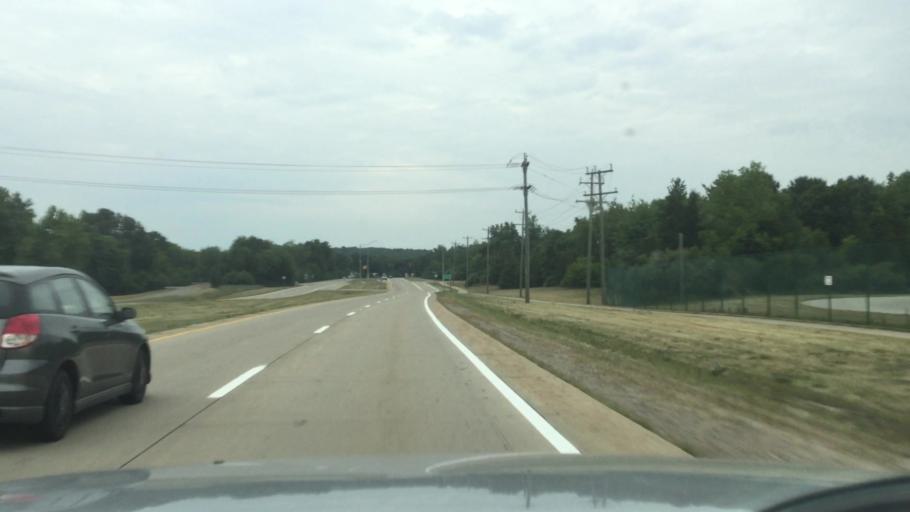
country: US
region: Michigan
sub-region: Oakland County
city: Waterford
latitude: 42.6664
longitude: -83.4385
